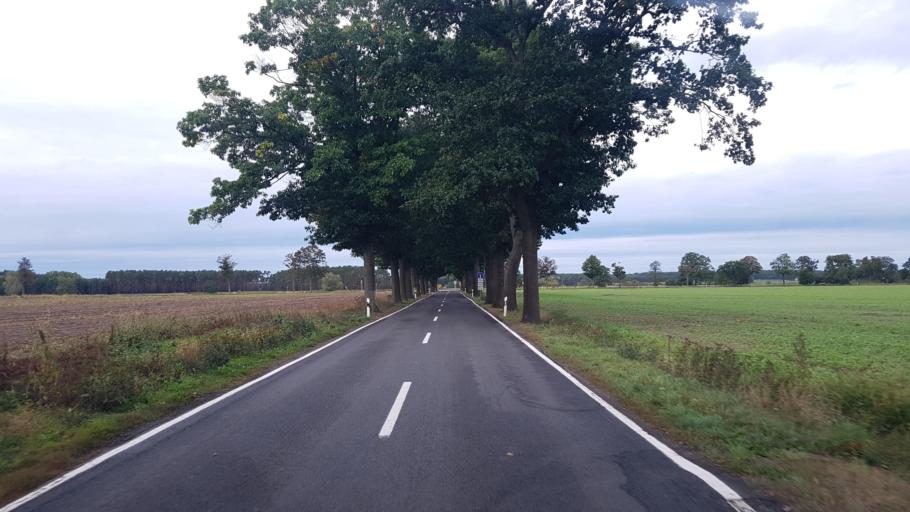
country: DE
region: Brandenburg
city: Kasel-Golzig
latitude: 51.9351
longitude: 13.6666
